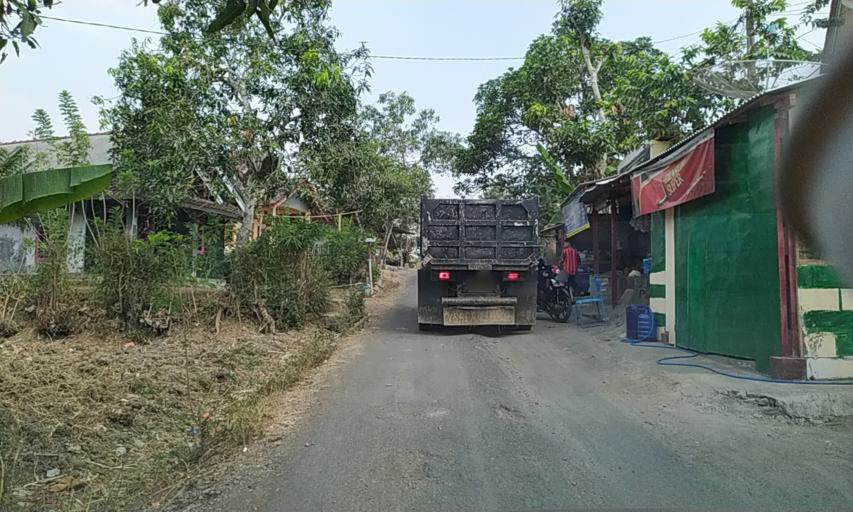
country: ID
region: Central Java
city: Karanggintung
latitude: -7.4648
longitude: 108.8828
